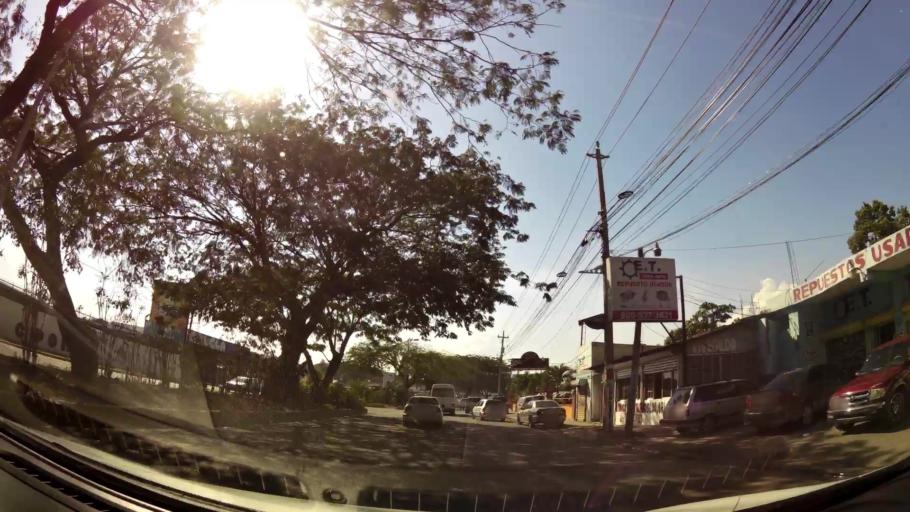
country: DO
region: San Cristobal
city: El Carril
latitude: 18.4608
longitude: -69.9911
